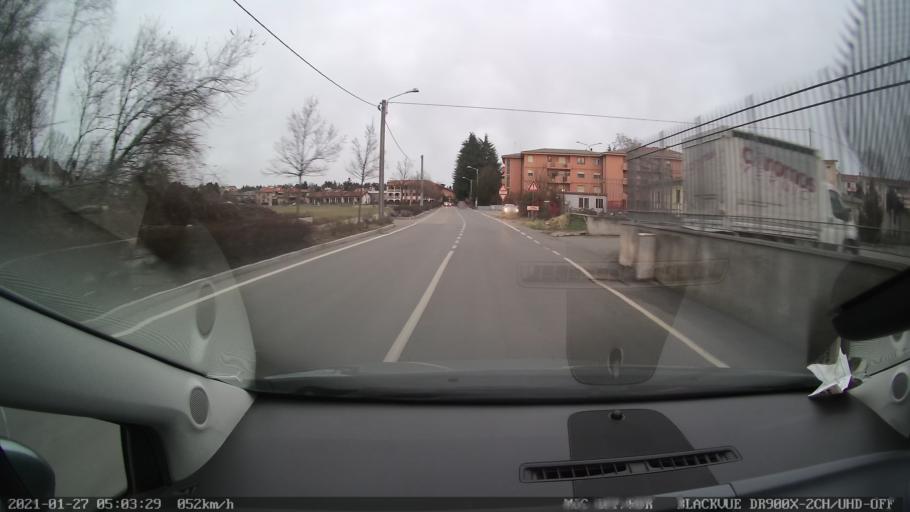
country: IT
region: Lombardy
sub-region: Provincia di Varese
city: Tradate
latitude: 45.7050
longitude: 8.9066
